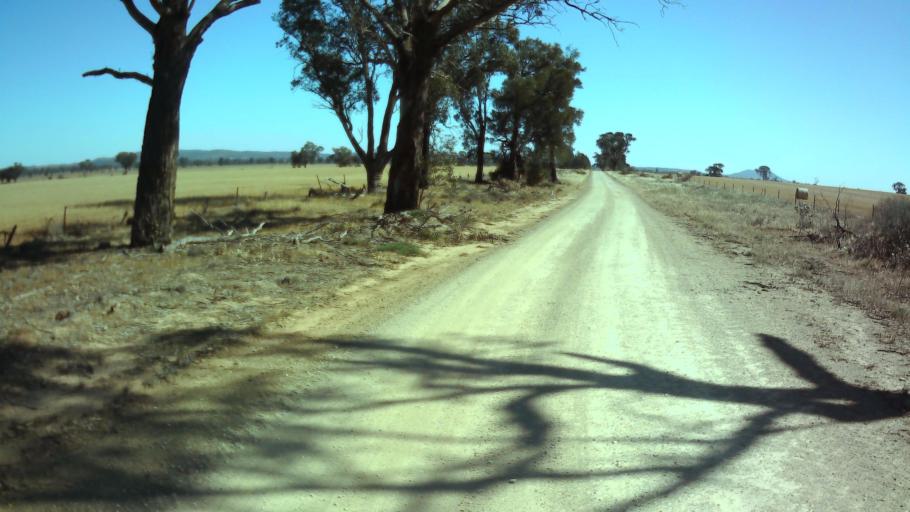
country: AU
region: New South Wales
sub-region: Weddin
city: Grenfell
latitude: -33.8787
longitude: 147.8736
